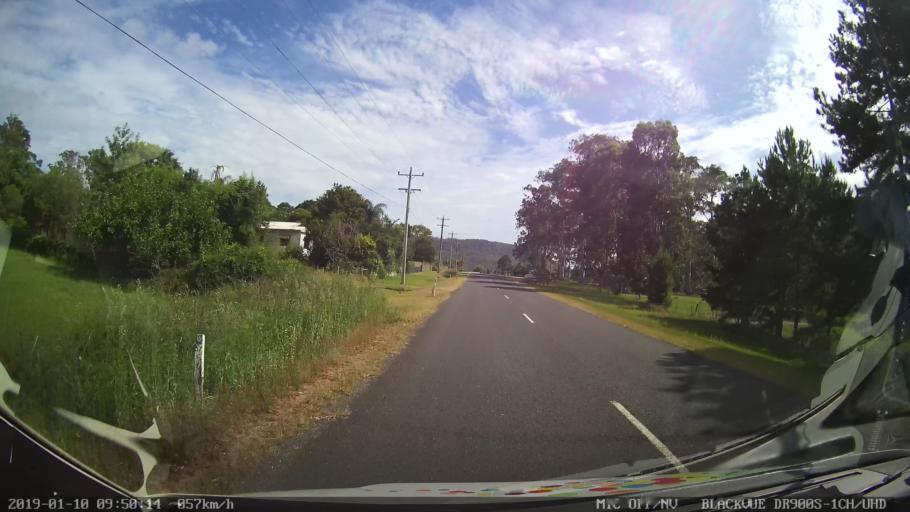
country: AU
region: New South Wales
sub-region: Coffs Harbour
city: Nana Glen
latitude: -30.0548
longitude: 152.9780
